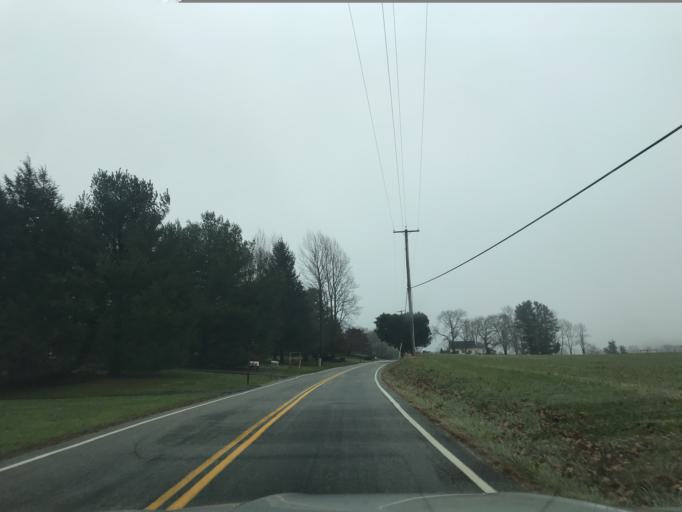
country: US
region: Maryland
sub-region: Harford County
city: South Bel Air
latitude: 39.5902
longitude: -76.2829
